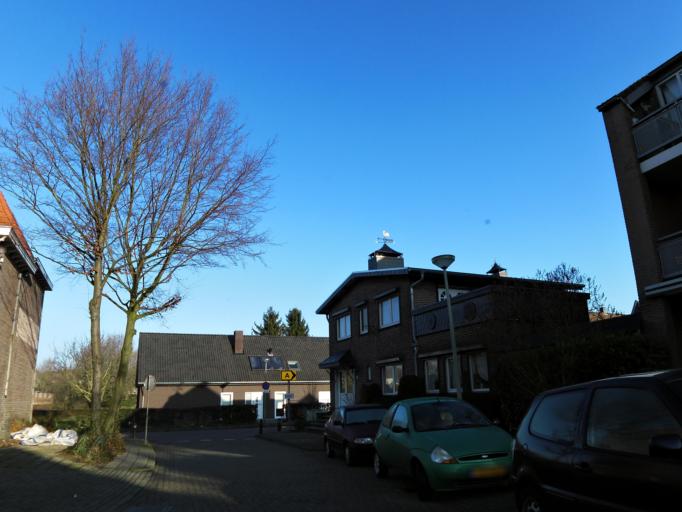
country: NL
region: Limburg
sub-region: Gemeente Kerkrade
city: Kerkrade
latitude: 50.9164
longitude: 6.0486
